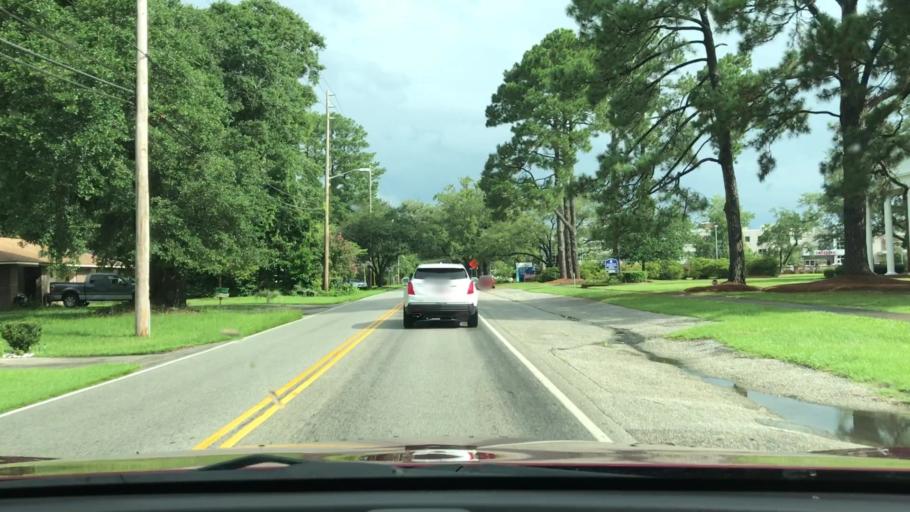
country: US
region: South Carolina
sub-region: Georgetown County
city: Georgetown
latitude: 33.3772
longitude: -79.2845
